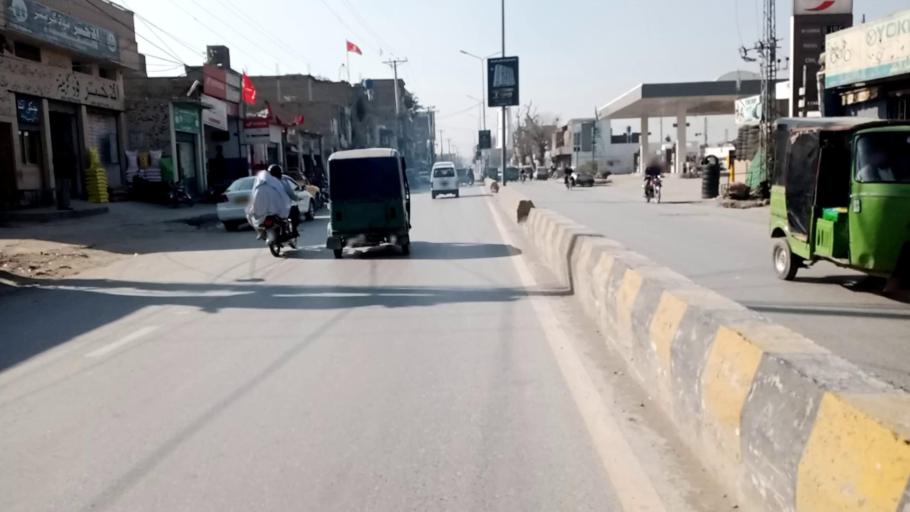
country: PK
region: Khyber Pakhtunkhwa
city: Peshawar
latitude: 33.9788
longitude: 71.5216
